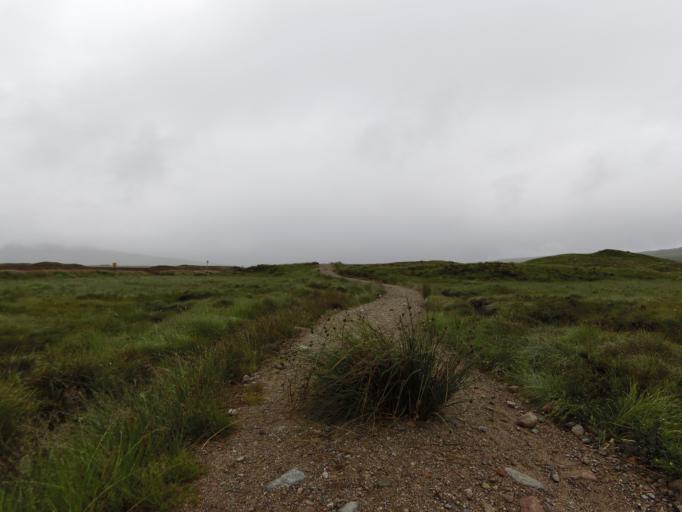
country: GB
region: Scotland
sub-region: Highland
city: Spean Bridge
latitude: 56.7634
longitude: -4.6972
